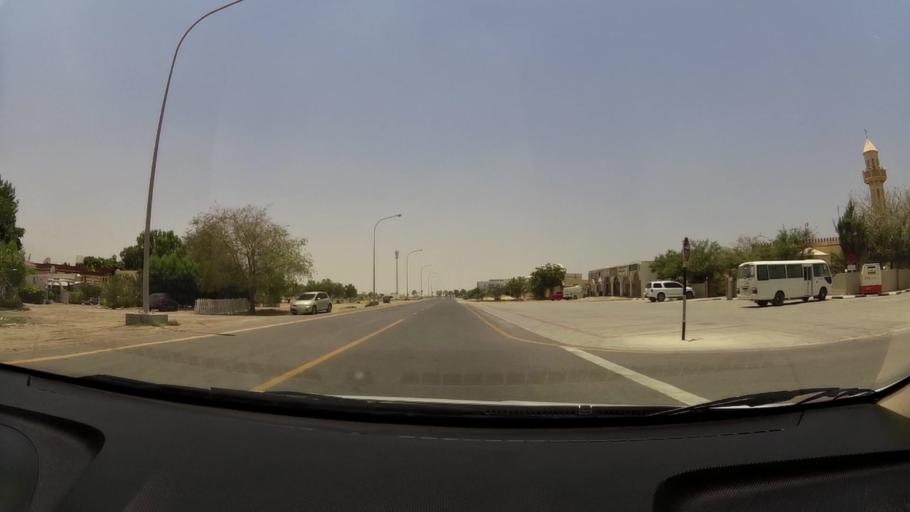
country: AE
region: Umm al Qaywayn
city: Umm al Qaywayn
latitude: 25.5346
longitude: 55.5424
